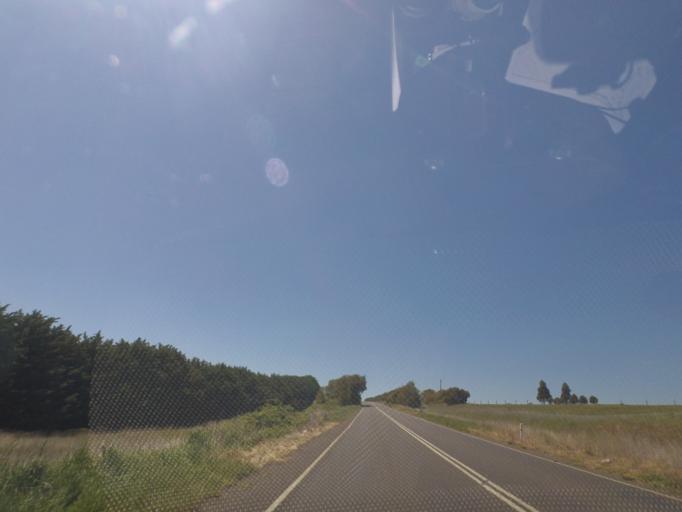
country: AU
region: Victoria
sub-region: Hume
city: Sunbury
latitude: -37.4215
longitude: 144.7377
